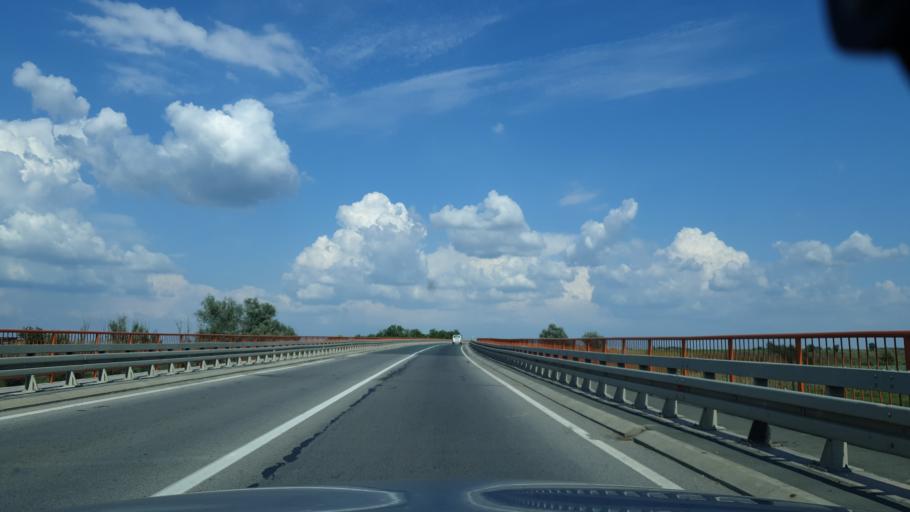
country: RS
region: Autonomna Pokrajina Vojvodina
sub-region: Juznobacki Okrug
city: Petrovaradin
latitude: 45.3071
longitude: 19.8685
